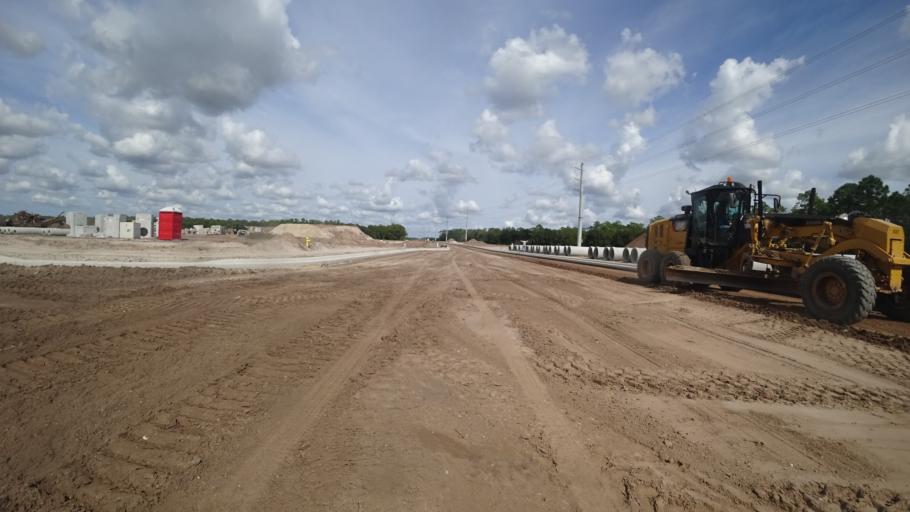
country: US
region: Florida
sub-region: Sarasota County
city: The Meadows
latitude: 27.4212
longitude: -82.3525
